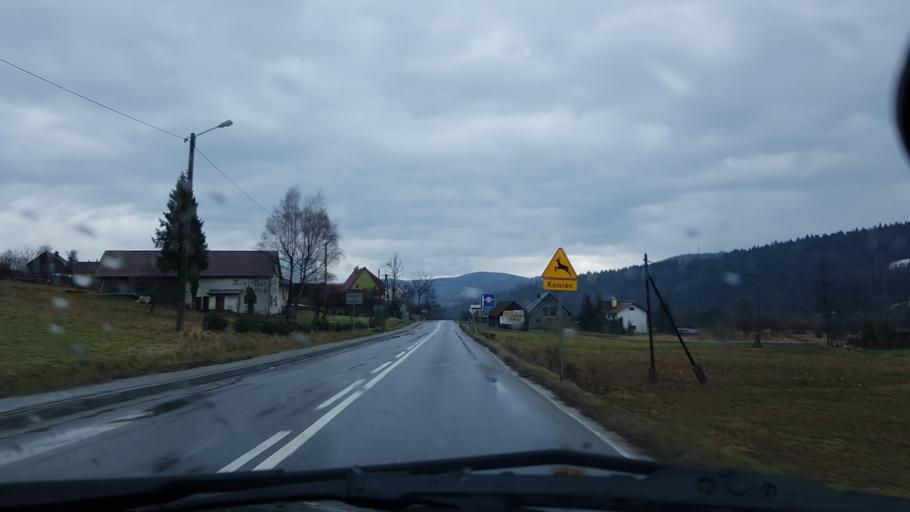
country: PL
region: Lesser Poland Voivodeship
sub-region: Powiat suski
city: Kukow
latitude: 49.7329
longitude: 19.4826
